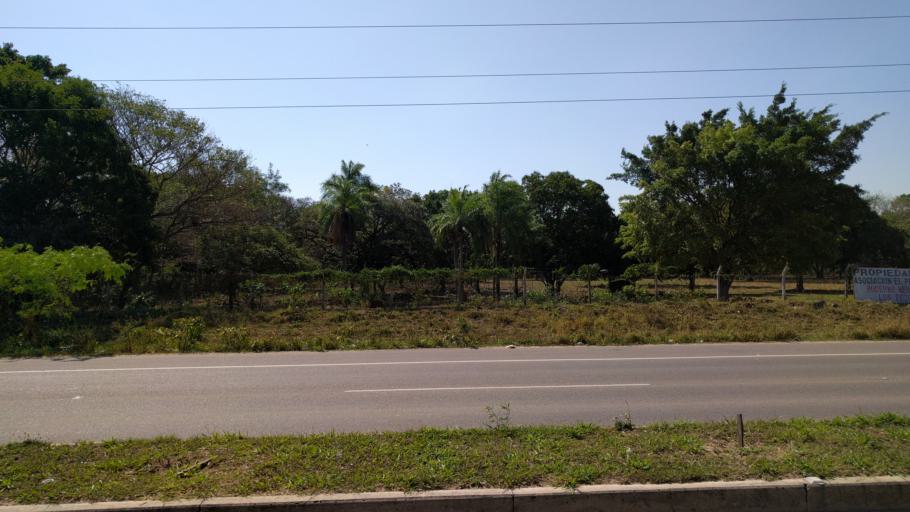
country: BO
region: Santa Cruz
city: Cotoca
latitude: -17.7581
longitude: -63.0088
